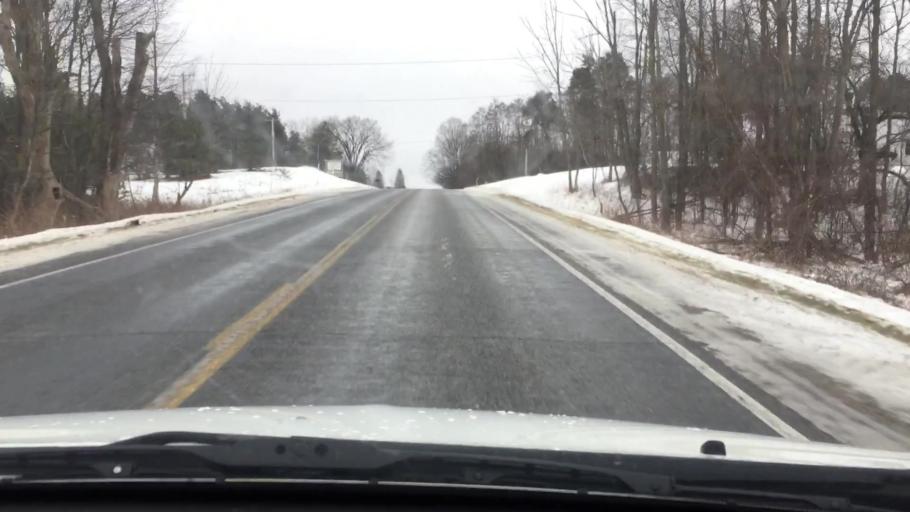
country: US
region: Michigan
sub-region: Wexford County
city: Cadillac
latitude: 44.0850
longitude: -85.4442
